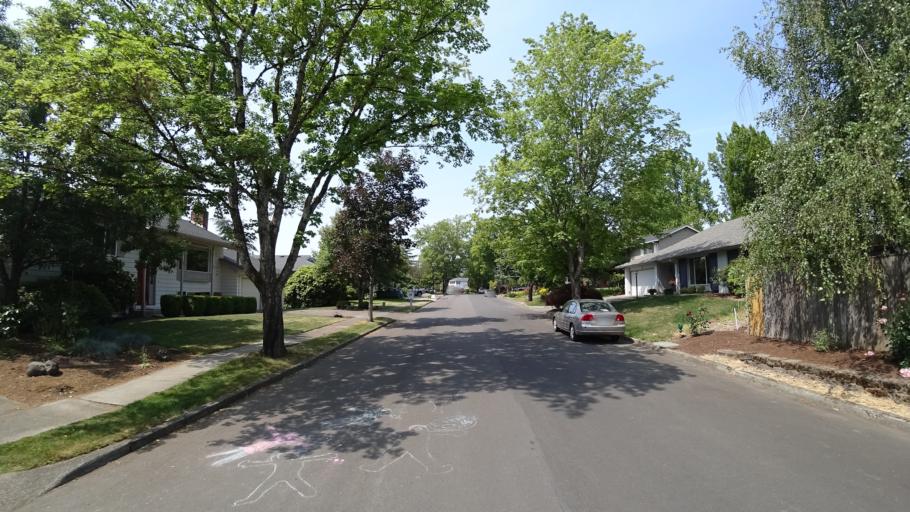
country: US
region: Oregon
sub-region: Washington County
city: Oak Hills
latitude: 45.5382
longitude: -122.8302
